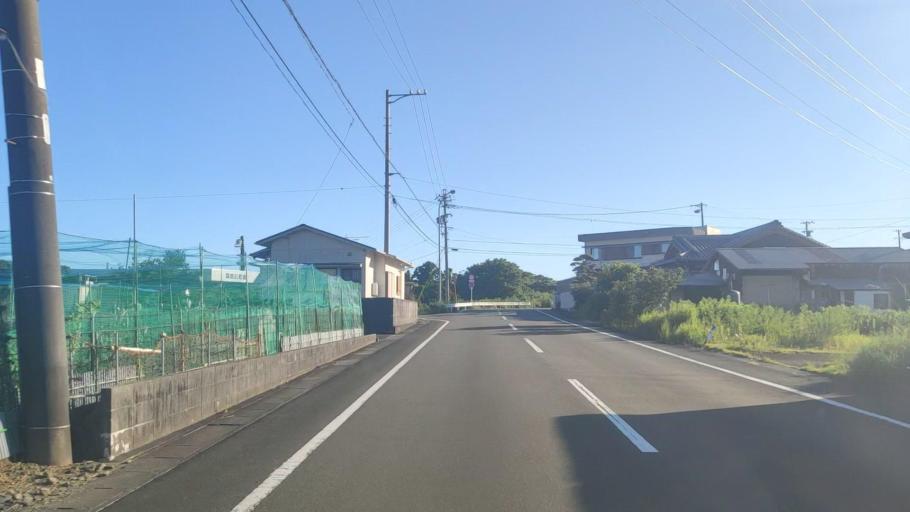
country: JP
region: Mie
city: Toba
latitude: 34.2867
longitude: 136.8913
